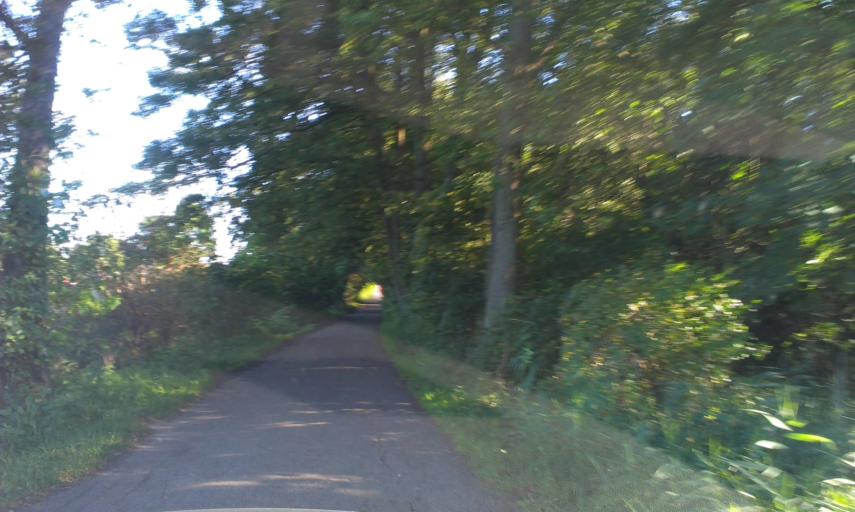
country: PL
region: West Pomeranian Voivodeship
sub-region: Powiat koszalinski
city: Bobolice
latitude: 53.8467
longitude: 16.6750
